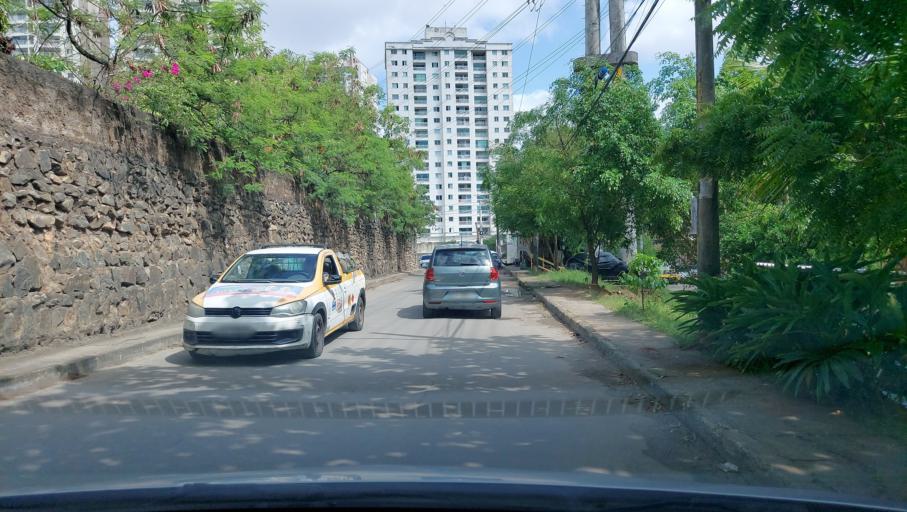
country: BR
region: Bahia
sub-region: Salvador
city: Salvador
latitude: -12.9658
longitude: -38.4298
